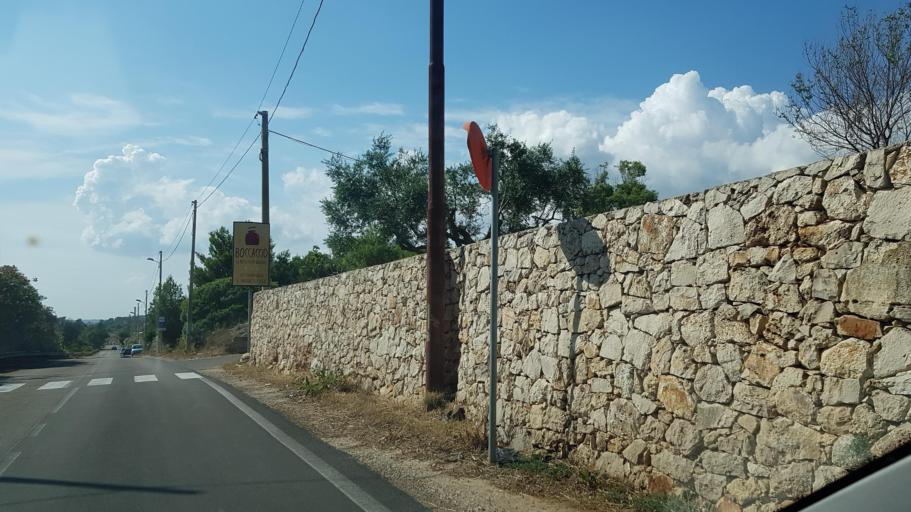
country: IT
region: Apulia
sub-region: Provincia di Lecce
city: Morciano di Leuca
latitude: 39.8152
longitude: 18.3126
